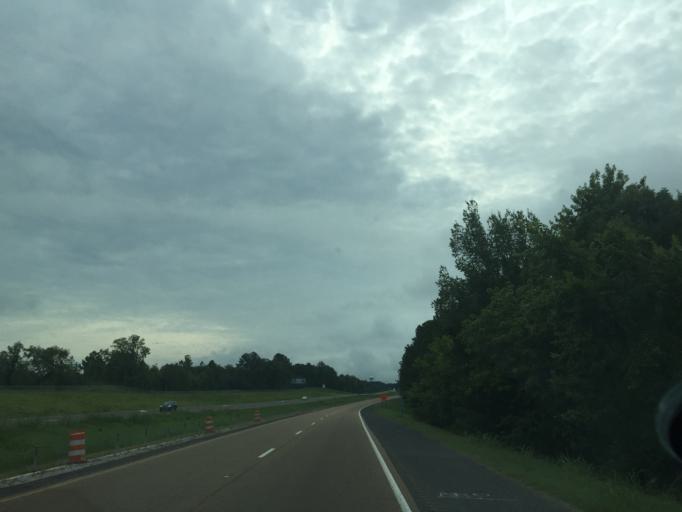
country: US
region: Mississippi
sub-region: Rankin County
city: Brandon
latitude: 32.2798
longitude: -90.0135
